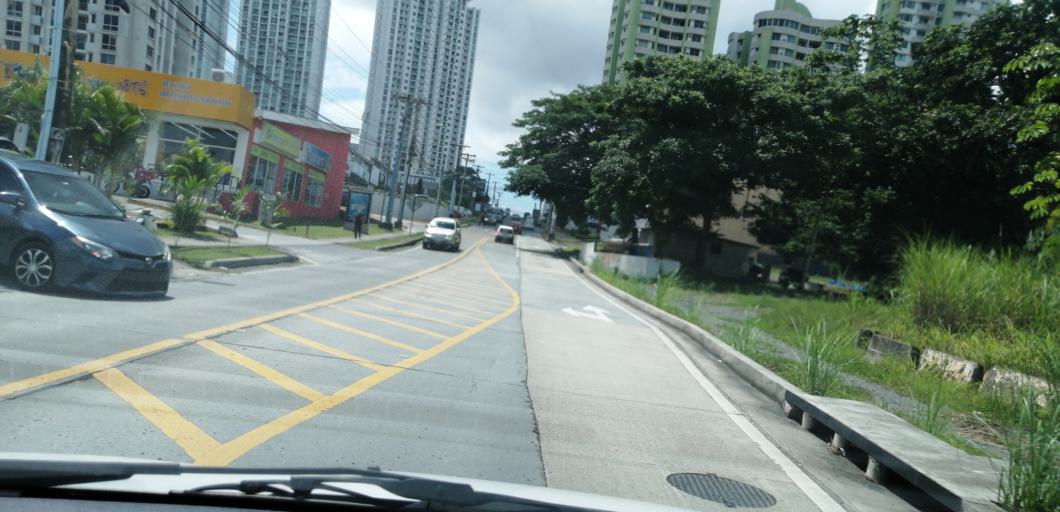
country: PA
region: Panama
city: Panama
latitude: 9.0297
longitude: -79.5255
